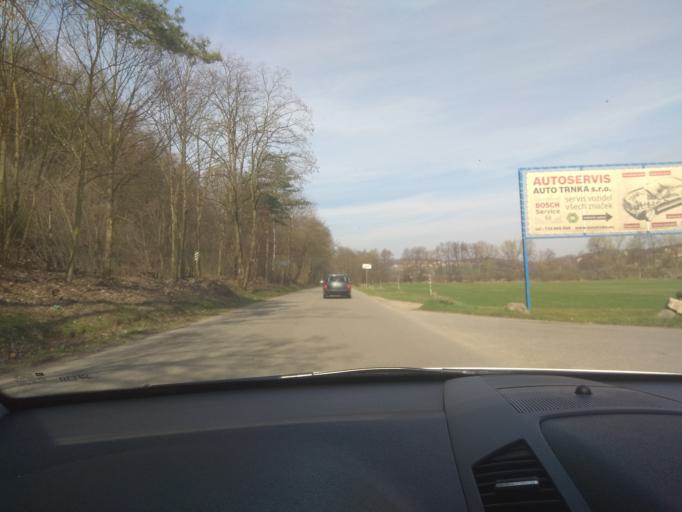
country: CZ
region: South Moravian
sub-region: Okres Brno-Venkov
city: Rosice
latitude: 49.1798
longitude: 16.3819
